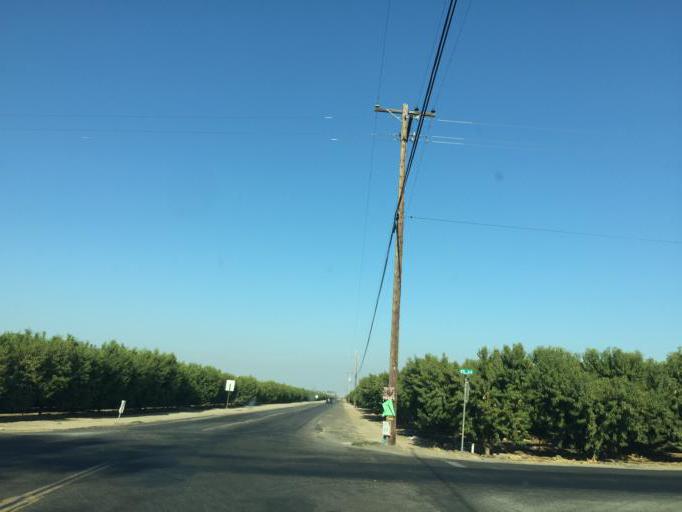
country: US
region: California
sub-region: Tulare County
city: London
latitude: 36.4589
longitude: -119.4749
